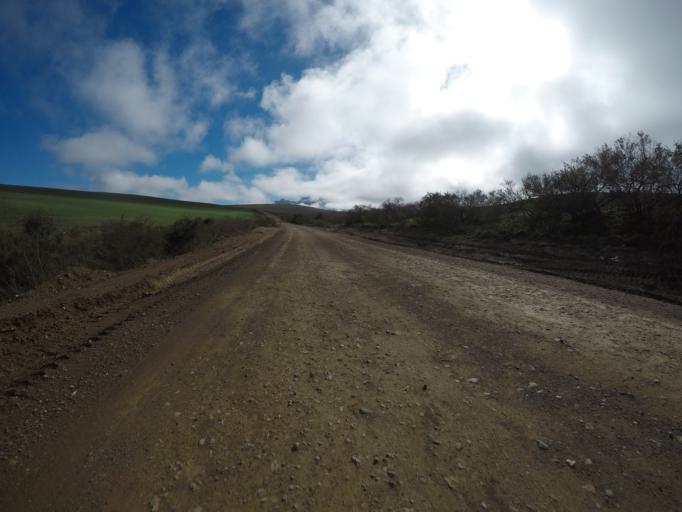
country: ZA
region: Western Cape
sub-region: Overberg District Municipality
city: Caledon
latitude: -34.1120
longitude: 19.7708
